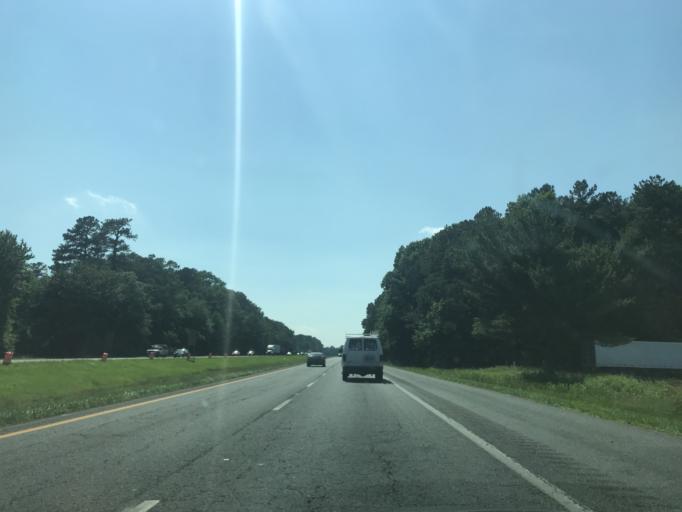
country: US
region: Maryland
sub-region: Wicomico County
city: Salisbury
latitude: 38.3925
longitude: -75.5494
